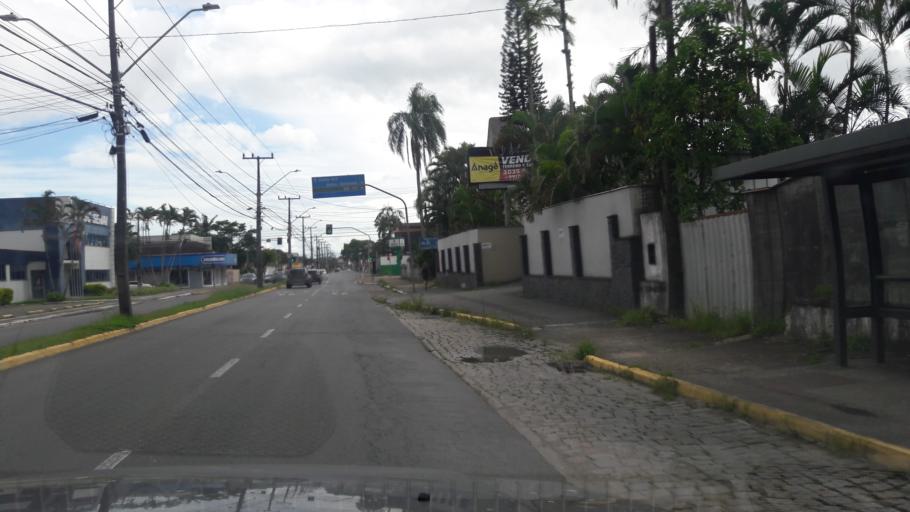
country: BR
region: Santa Catarina
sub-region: Joinville
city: Joinville
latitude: -26.3136
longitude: -48.8407
